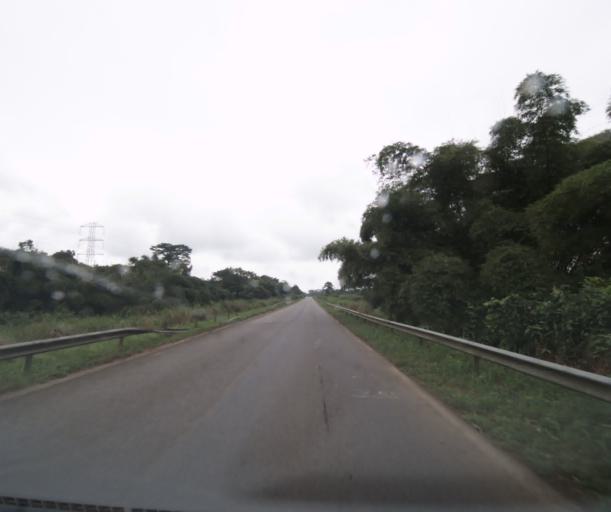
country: CM
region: Littoral
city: Edea
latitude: 3.7053
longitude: 10.1067
